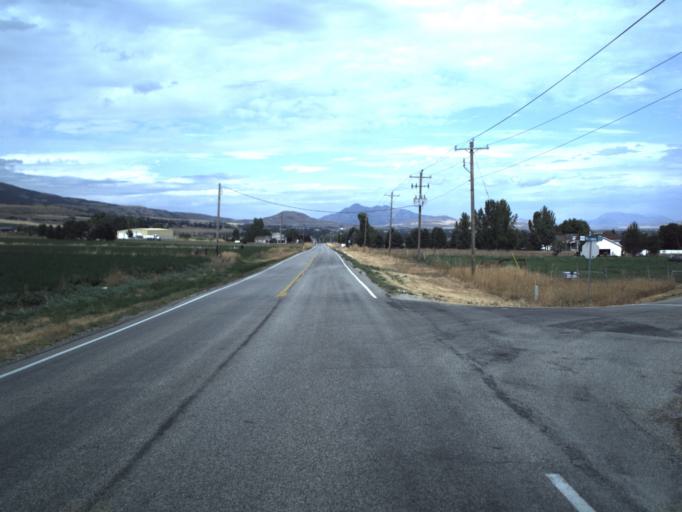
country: US
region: Utah
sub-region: Cache County
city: Wellsville
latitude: 41.6648
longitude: -111.9493
